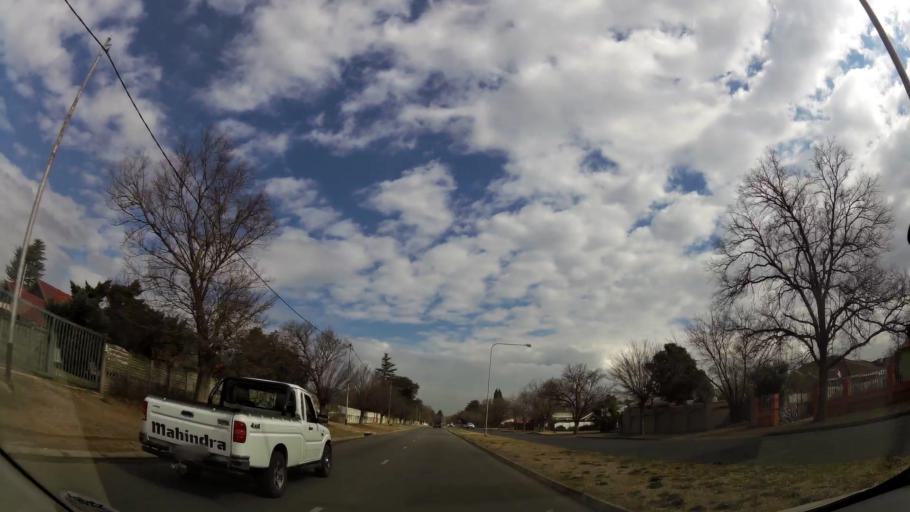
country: ZA
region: Gauteng
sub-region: Sedibeng District Municipality
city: Vereeniging
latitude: -26.6600
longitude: 27.9839
